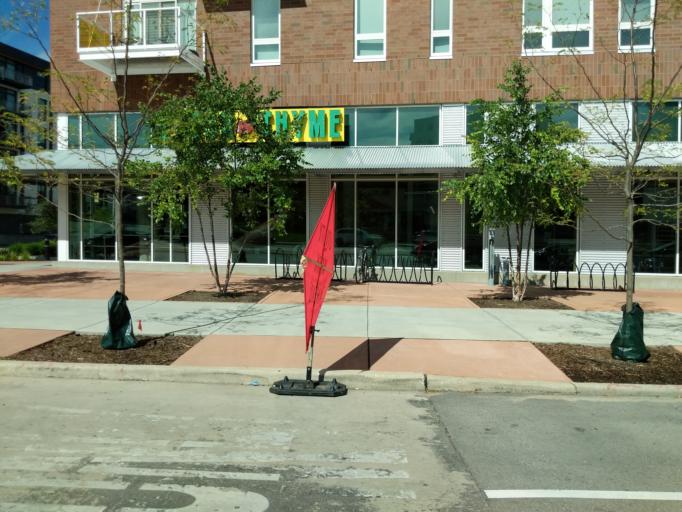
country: US
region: Wisconsin
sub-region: Milwaukee County
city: Milwaukee
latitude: 43.0512
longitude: -87.9061
